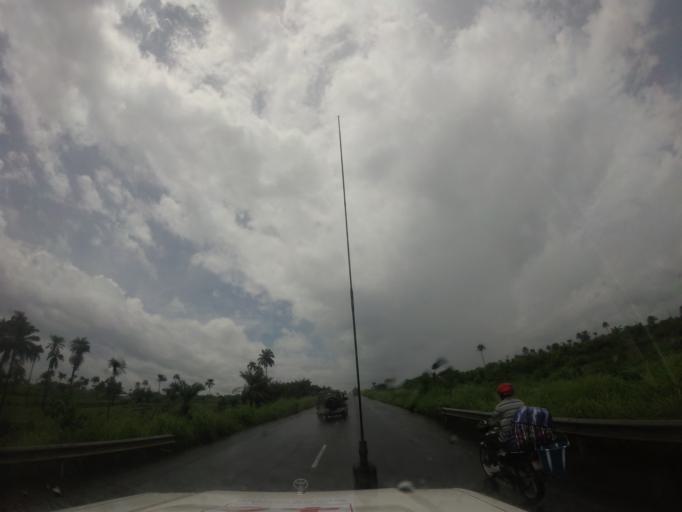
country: SL
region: Southern Province
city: Rotifunk
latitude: 8.4871
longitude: -12.7729
